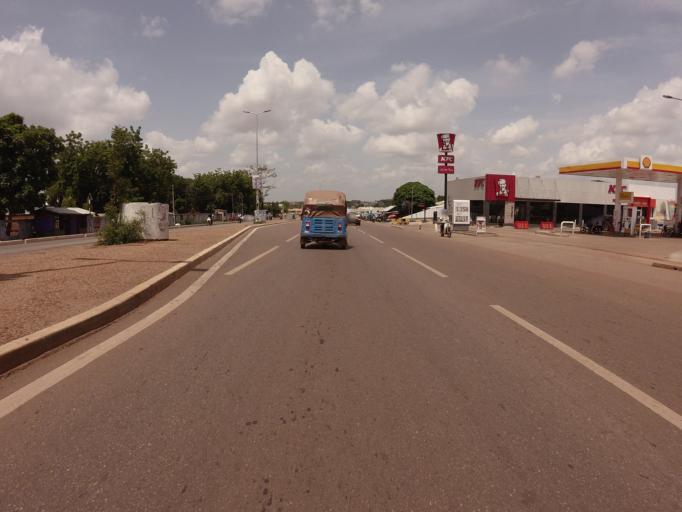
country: GH
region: Northern
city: Tamale
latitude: 9.4001
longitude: -0.8341
